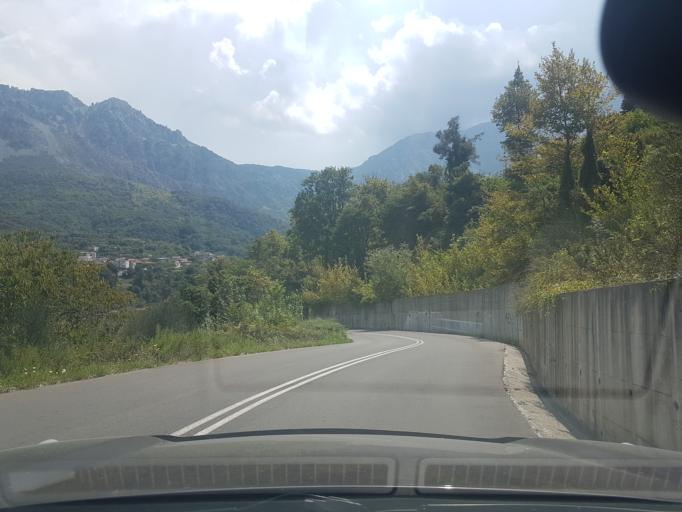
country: GR
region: Central Greece
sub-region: Nomos Evvoias
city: Kymi
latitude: 38.6285
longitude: 23.9455
